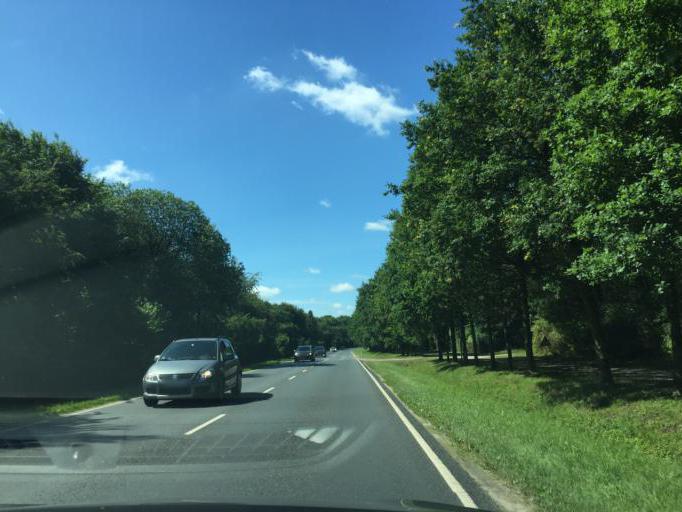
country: DK
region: South Denmark
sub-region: Odense Kommune
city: Odense
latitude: 55.3802
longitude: 10.3448
